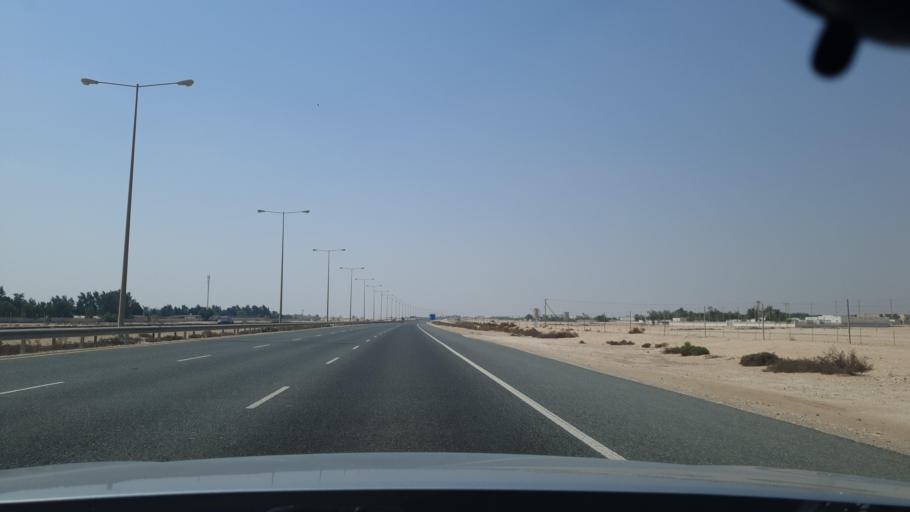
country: QA
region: Al Khawr
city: Al Khawr
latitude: 25.7555
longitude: 51.4541
